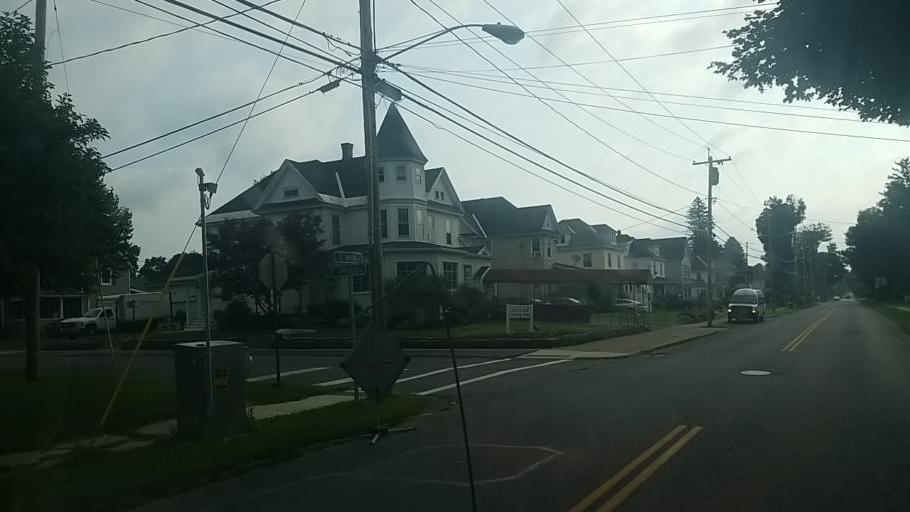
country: US
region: New York
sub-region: Fulton County
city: Johnstown
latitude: 43.0072
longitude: -74.3622
